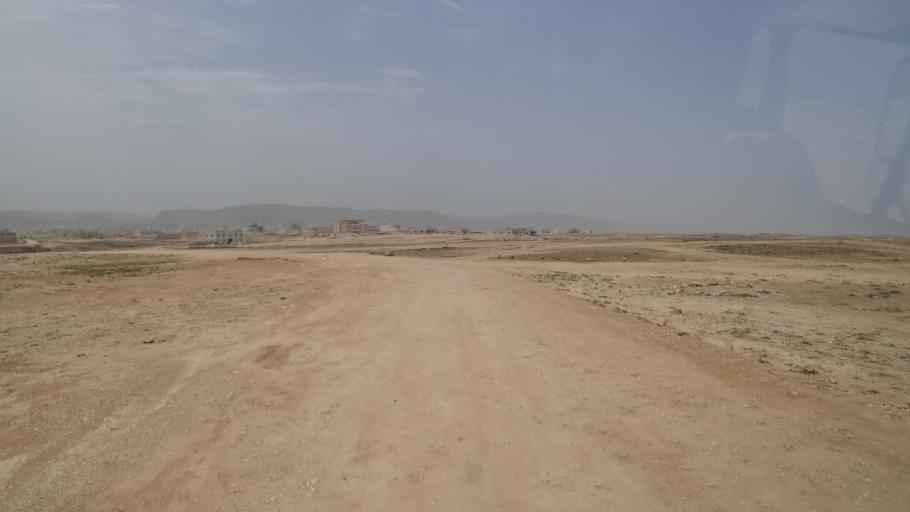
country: OM
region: Zufar
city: Salalah
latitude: 17.0355
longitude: 54.4094
